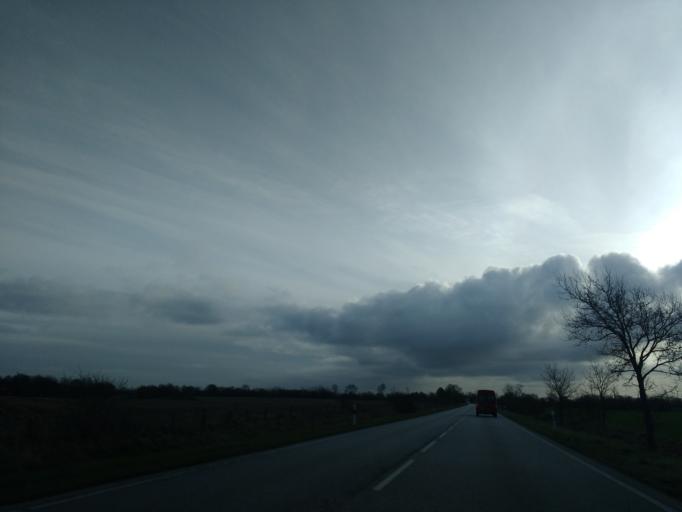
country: DE
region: Schleswig-Holstein
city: Krogaspe
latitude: 54.1329
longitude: 9.9131
